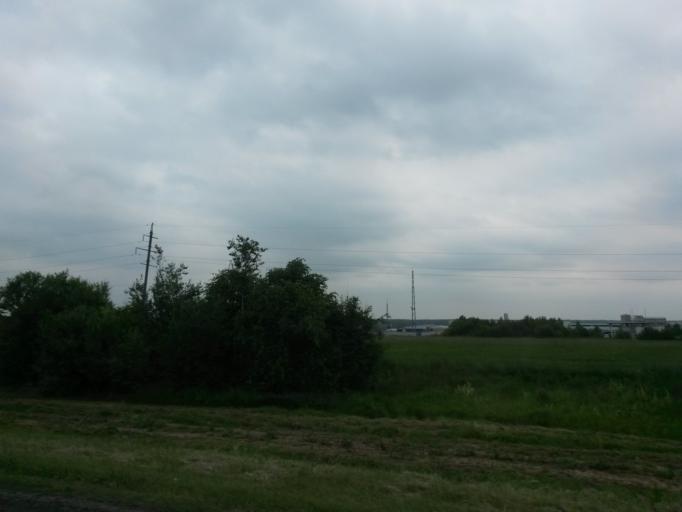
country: RU
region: Moskovskaya
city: Lyubuchany
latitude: 55.2560
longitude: 37.5321
